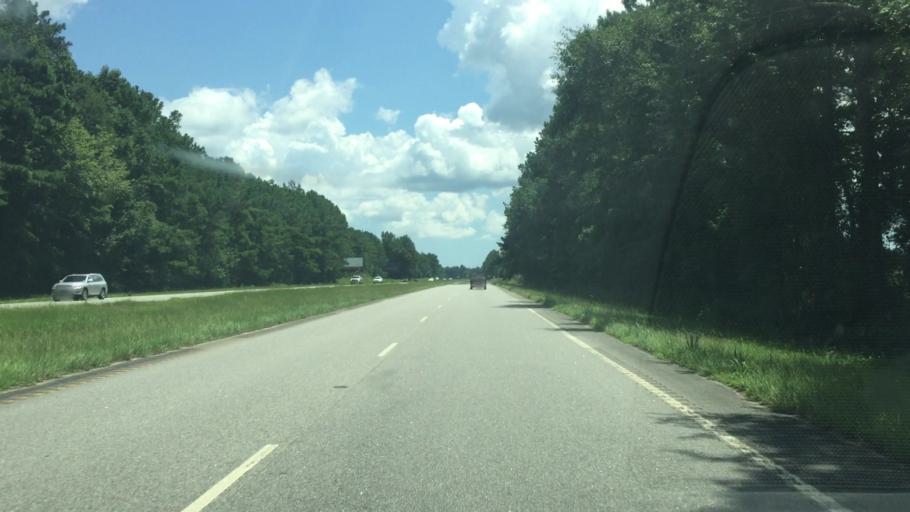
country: US
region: South Carolina
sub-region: Horry County
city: Loris
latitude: 34.0297
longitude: -78.8025
